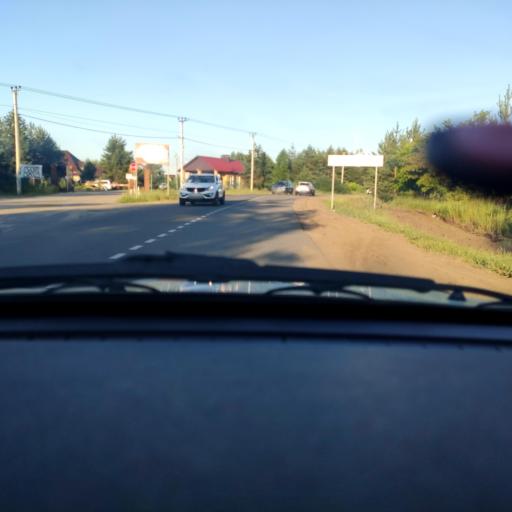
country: RU
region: Voronezj
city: Ramon'
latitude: 51.8922
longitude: 39.2421
